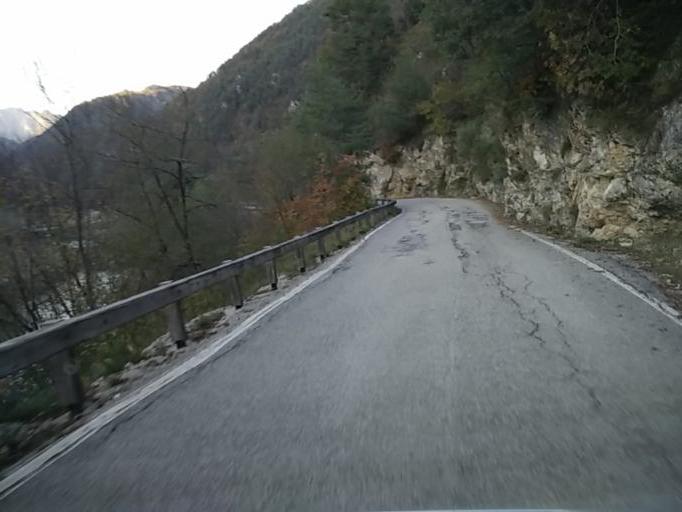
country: IT
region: Lombardy
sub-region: Provincia di Brescia
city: Valvestino
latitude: 45.7197
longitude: 10.6119
